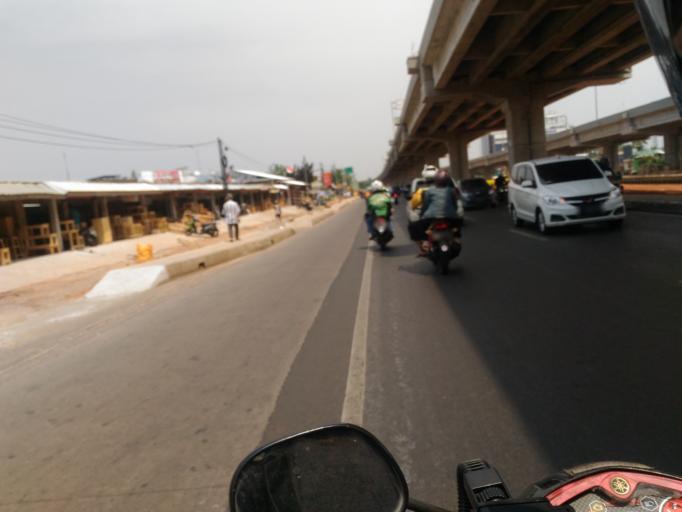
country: ID
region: Jakarta Raya
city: Jakarta
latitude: -6.2404
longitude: 106.8950
